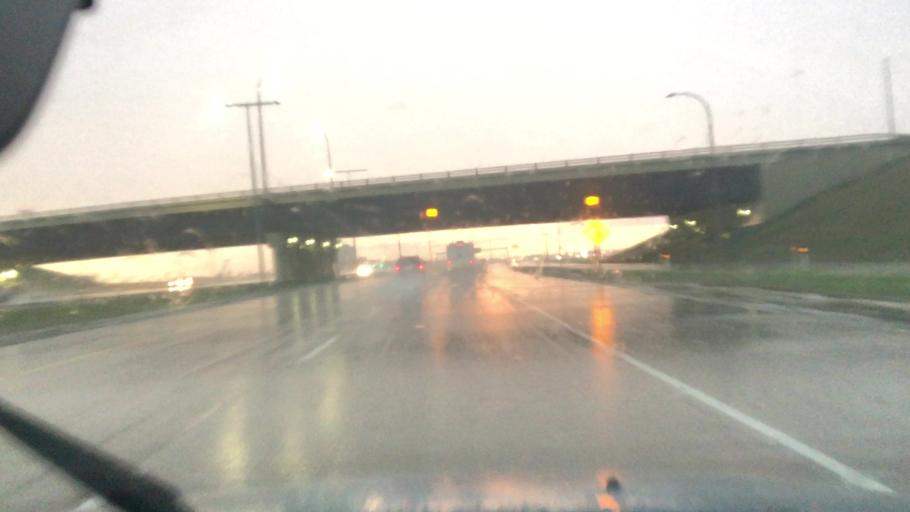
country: CA
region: Alberta
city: Edmonton
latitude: 53.4304
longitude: -113.5813
